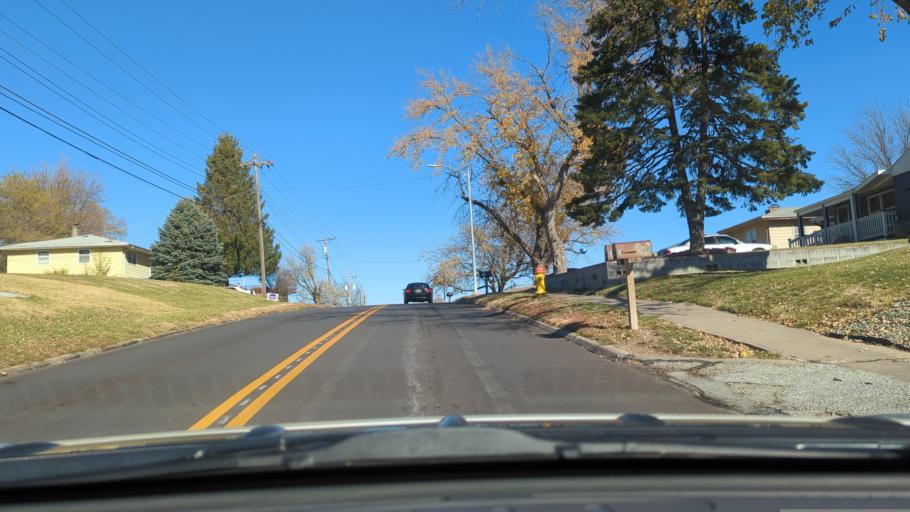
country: US
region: Nebraska
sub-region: Sarpy County
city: La Vista
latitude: 41.1894
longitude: -95.9770
